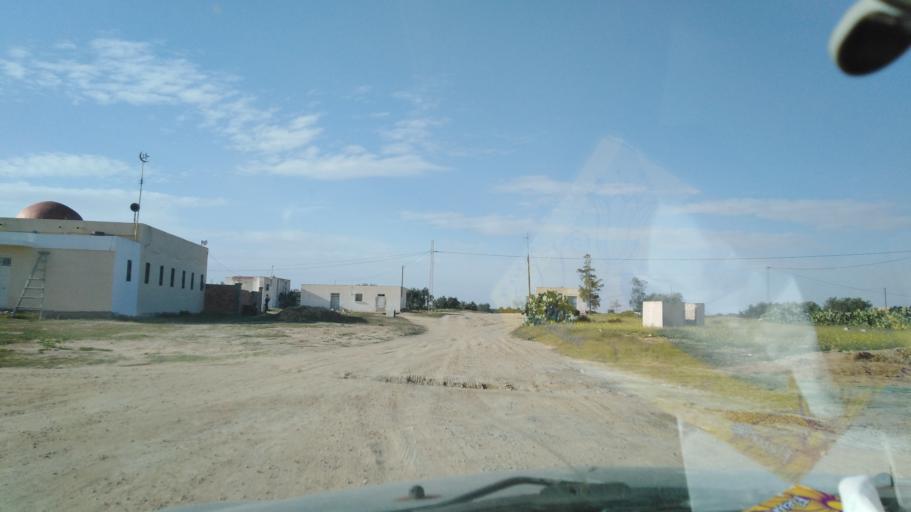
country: TN
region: Safaqis
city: Bi'r `Ali Bin Khalifah
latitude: 34.6625
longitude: 10.3208
